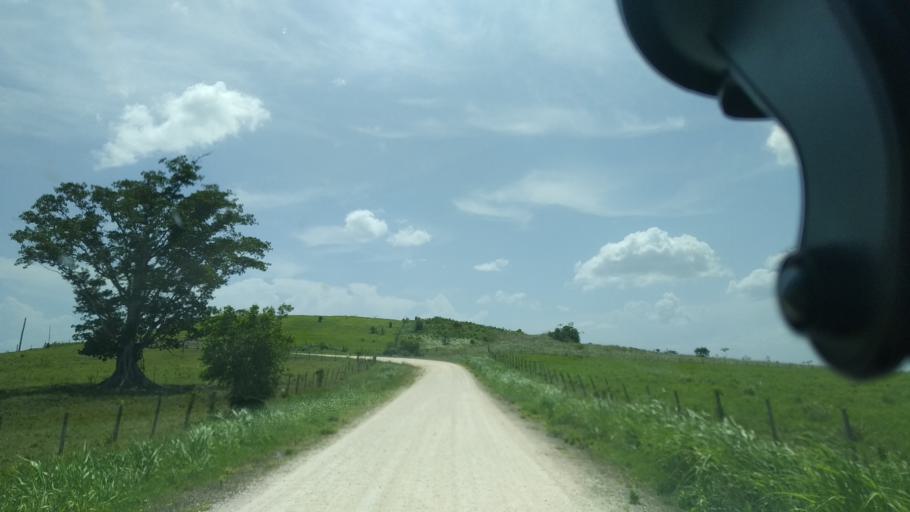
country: BZ
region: Cayo
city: San Ignacio
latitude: 17.3001
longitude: -89.0560
